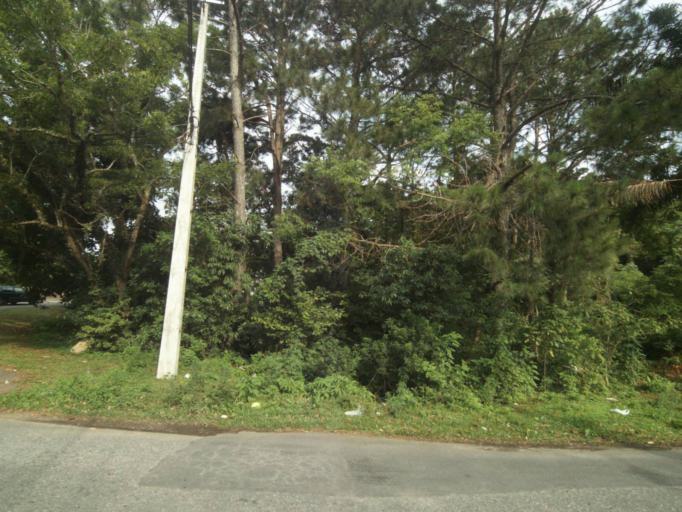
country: BR
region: Parana
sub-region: Curitiba
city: Curitiba
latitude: -25.4106
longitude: -49.3073
